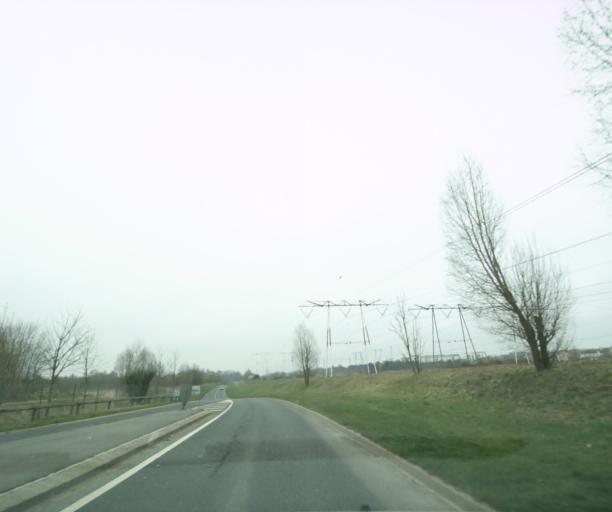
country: FR
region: Ile-de-France
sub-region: Departement du Val-d'Oise
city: Courdimanche
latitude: 49.0493
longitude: 1.9964
